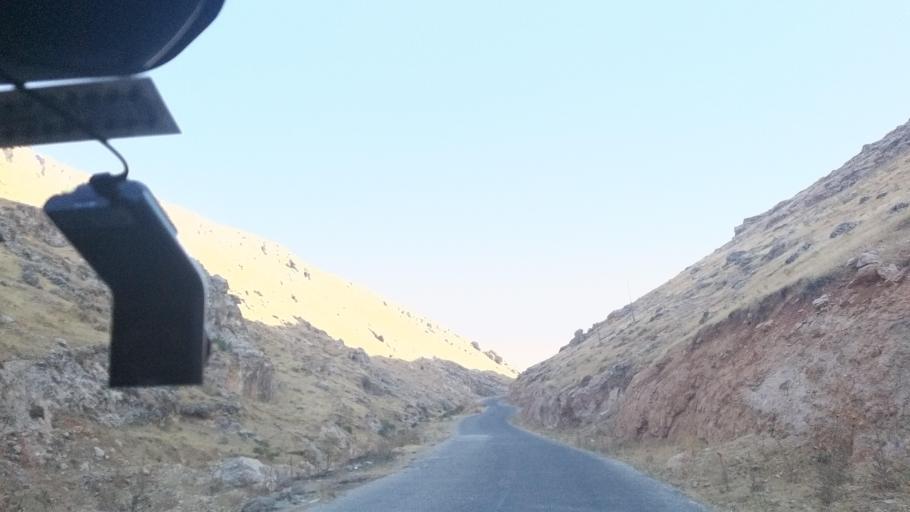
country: TR
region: Diyarbakir
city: Silvan
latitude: 38.1628
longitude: 41.0018
